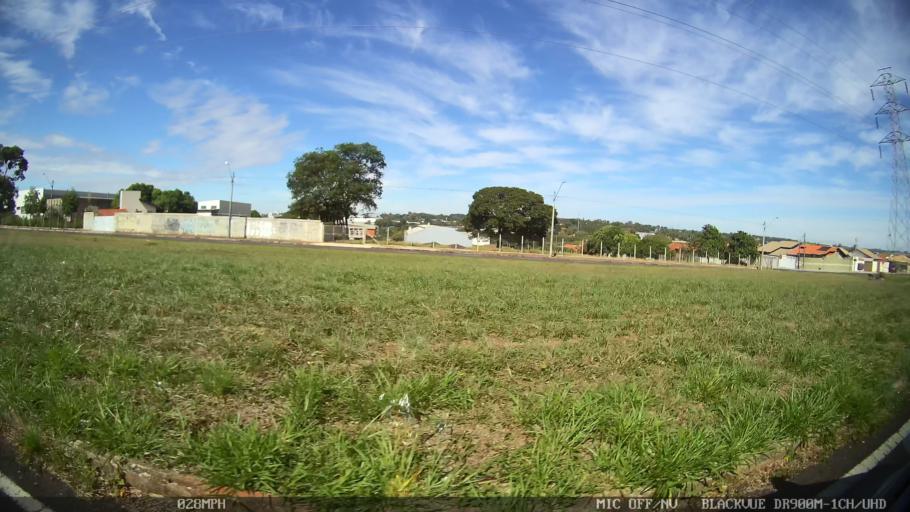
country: BR
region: Sao Paulo
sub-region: Sao Jose Do Rio Preto
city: Sao Jose do Rio Preto
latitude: -20.8389
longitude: -49.3575
